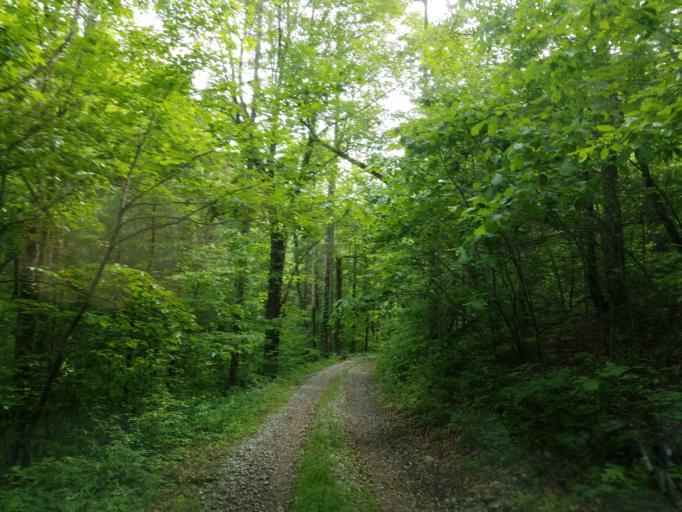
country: US
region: Georgia
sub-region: Union County
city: Blairsville
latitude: 34.7441
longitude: -84.0135
